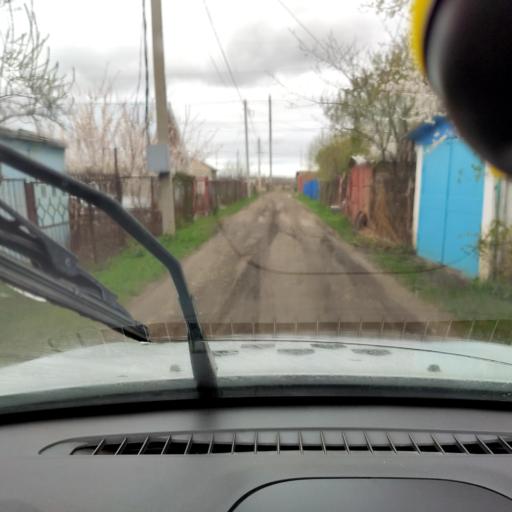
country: RU
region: Samara
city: Tol'yatti
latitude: 53.5862
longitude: 49.3166
